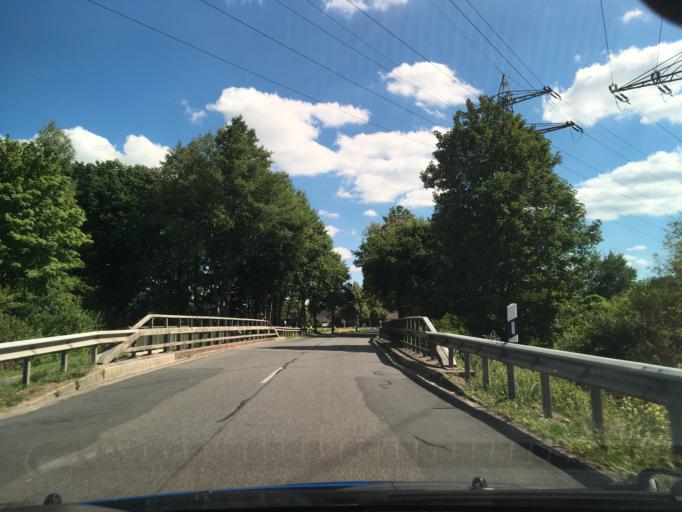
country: DE
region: Lower Saxony
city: Celle
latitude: 52.6256
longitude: 10.1203
